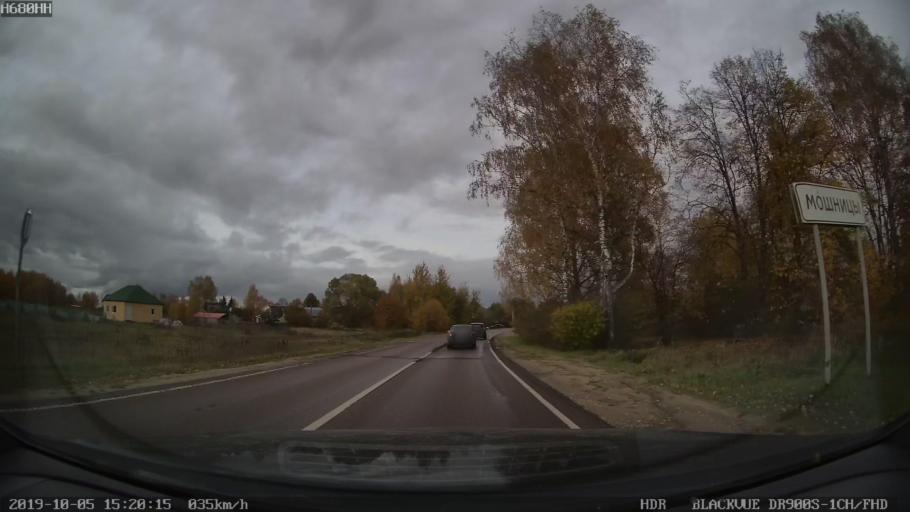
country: RU
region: Moskovskaya
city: Solnechnogorsk
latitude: 56.2221
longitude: 36.9048
